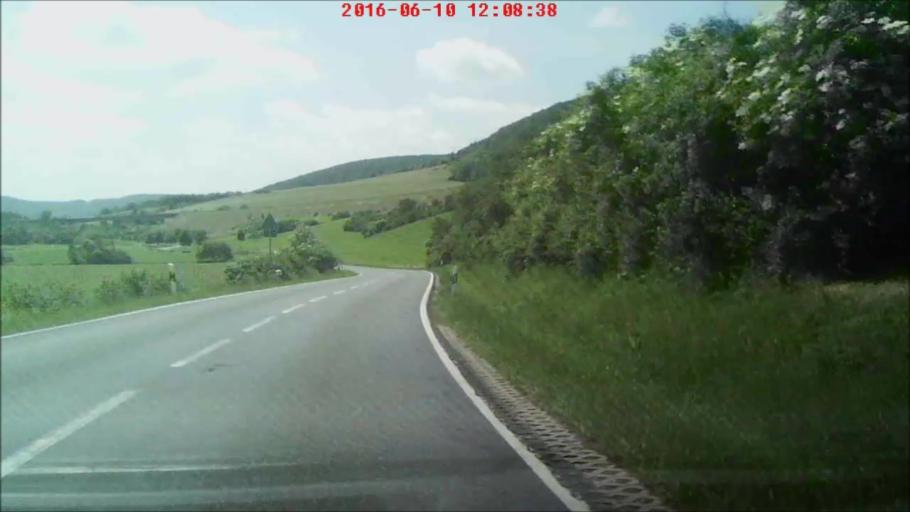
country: DE
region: Thuringia
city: Ellingshausen
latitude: 50.5619
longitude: 10.4789
